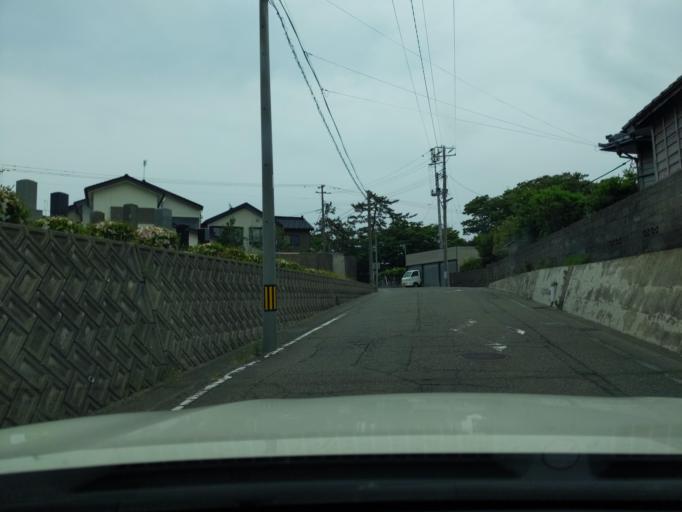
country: JP
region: Niigata
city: Kashiwazaki
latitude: 37.3625
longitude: 138.5410
